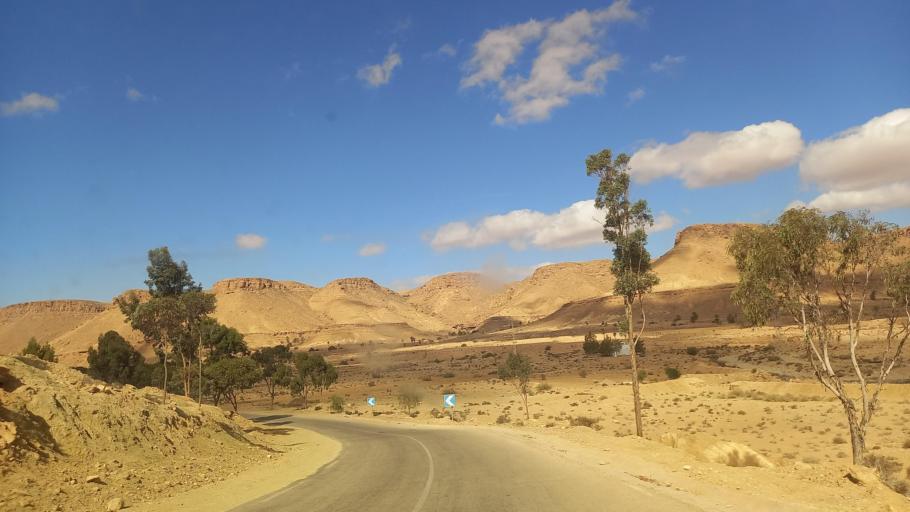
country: TN
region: Tataouine
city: Tataouine
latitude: 32.9167
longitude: 10.2748
